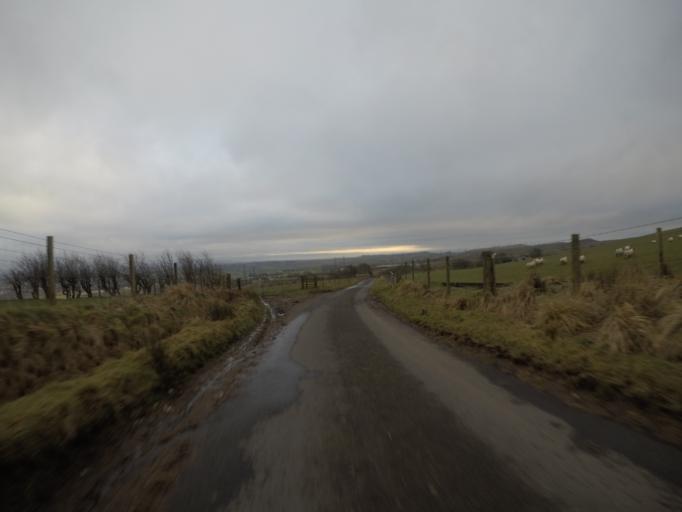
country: GB
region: Scotland
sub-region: North Ayrshire
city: Dalry
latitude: 55.7277
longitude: -4.7636
